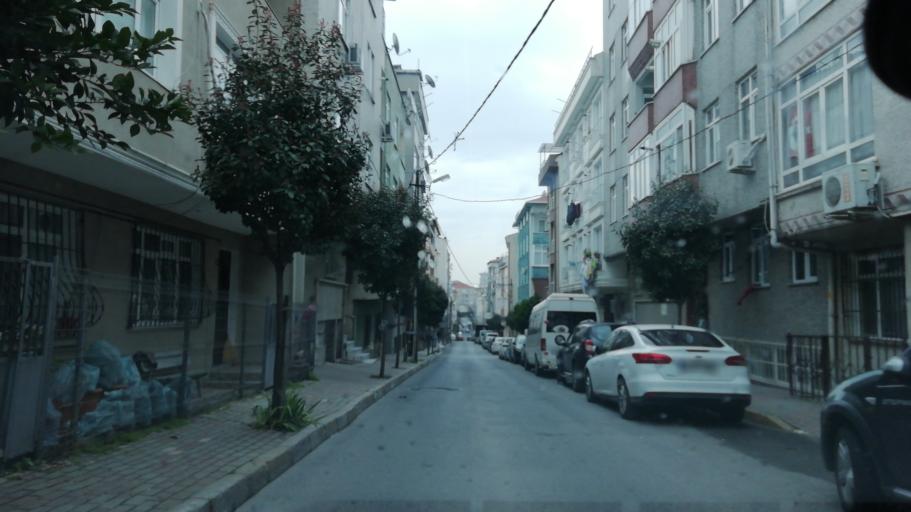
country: TR
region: Istanbul
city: Bagcilar
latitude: 41.0248
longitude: 28.8322
